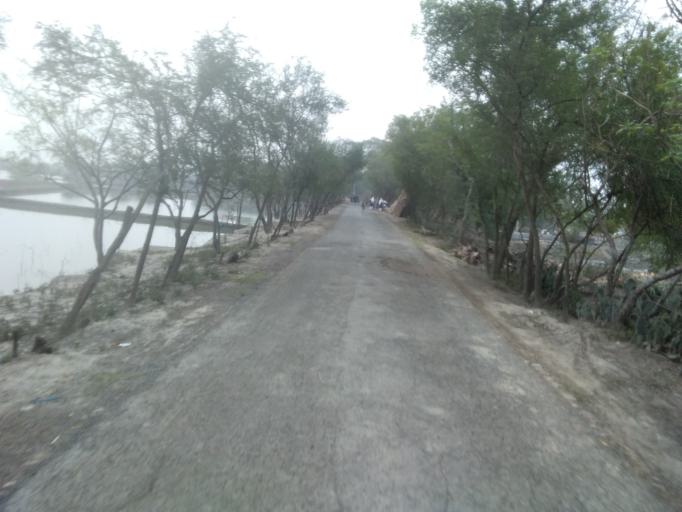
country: BD
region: Khulna
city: Satkhira
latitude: 22.5790
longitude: 89.0701
